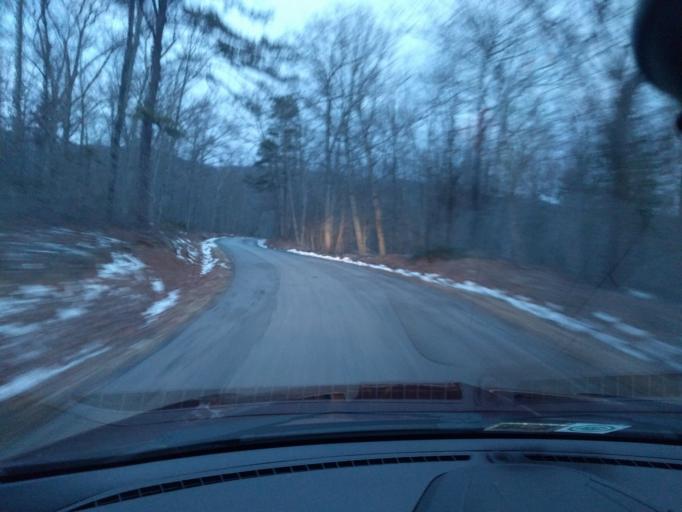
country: US
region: Virginia
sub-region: Alleghany County
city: Clifton Forge
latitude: 37.8616
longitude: -79.8762
